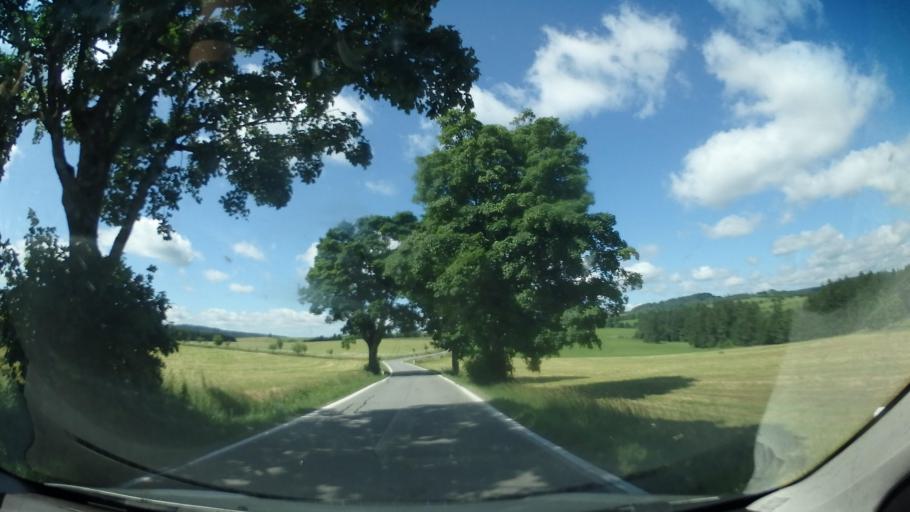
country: CZ
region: Vysocina
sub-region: Okres Zd'ar nad Sazavou
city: Nove Mesto na Morave
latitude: 49.6451
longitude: 16.1079
